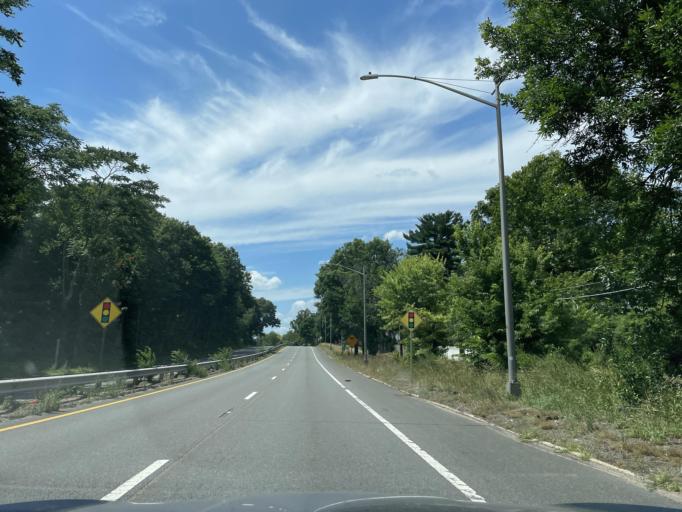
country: US
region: Massachusetts
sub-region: Norfolk County
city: Wellesley
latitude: 42.3143
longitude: -71.2635
